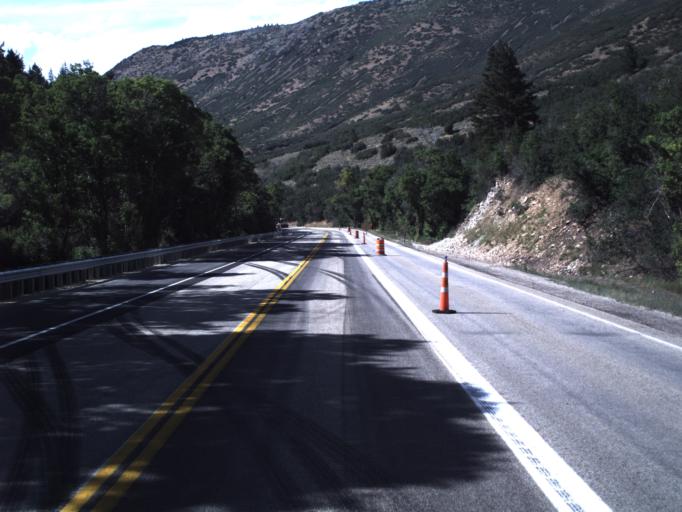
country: US
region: Utah
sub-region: Wasatch County
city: Heber
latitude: 40.3982
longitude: -111.3042
